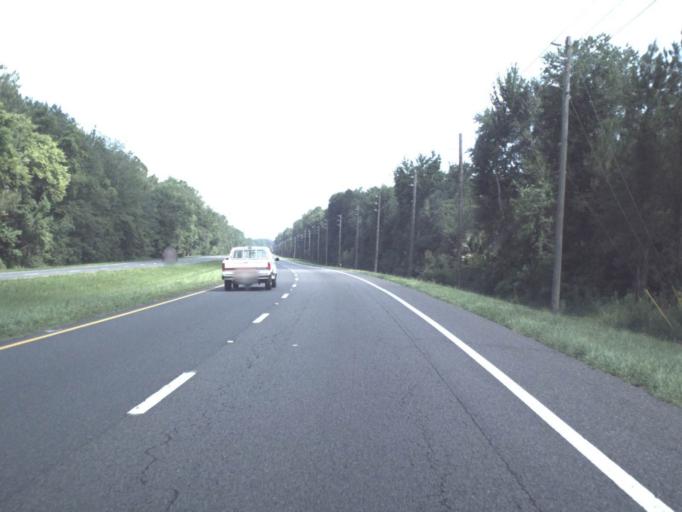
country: US
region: Florida
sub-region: Nassau County
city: Callahan
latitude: 30.6325
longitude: -81.8542
